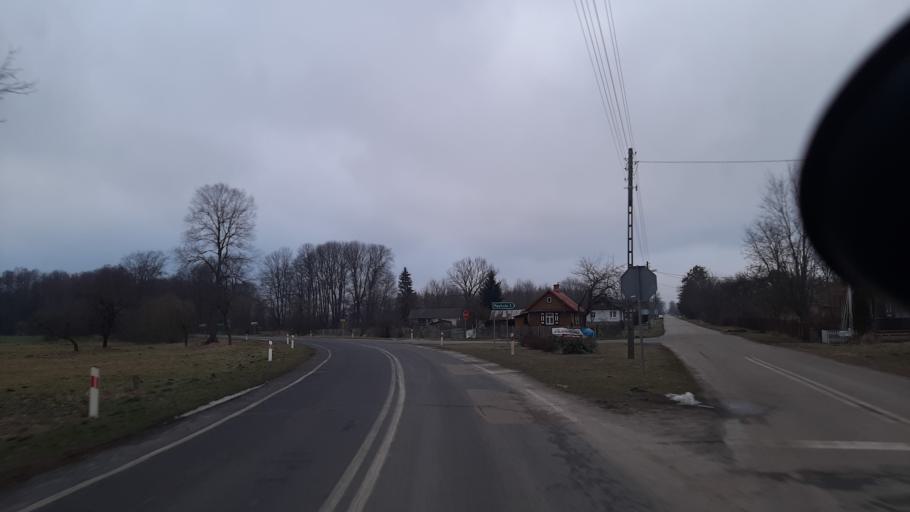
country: PL
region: Lublin Voivodeship
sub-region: Powiat parczewski
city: Sosnowica
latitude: 51.6128
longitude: 23.1220
